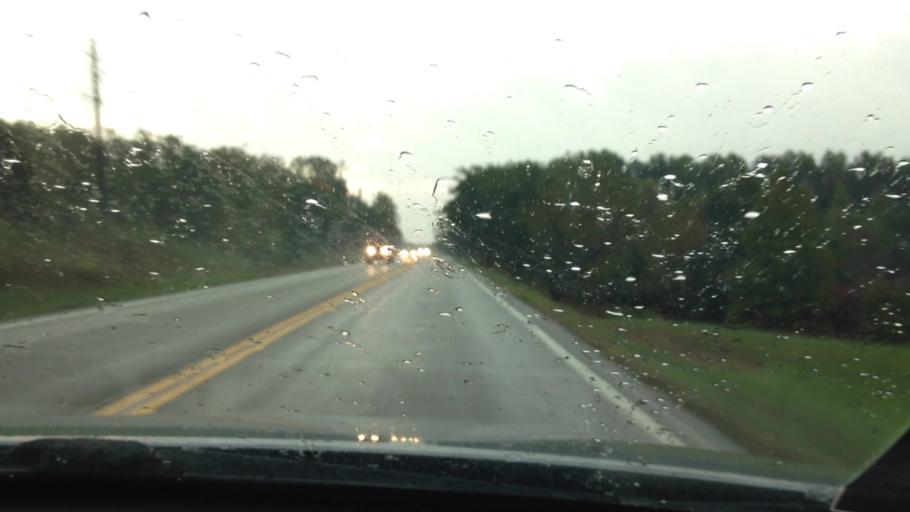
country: US
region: Missouri
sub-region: Platte County
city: Platte City
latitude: 39.3825
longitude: -94.8151
